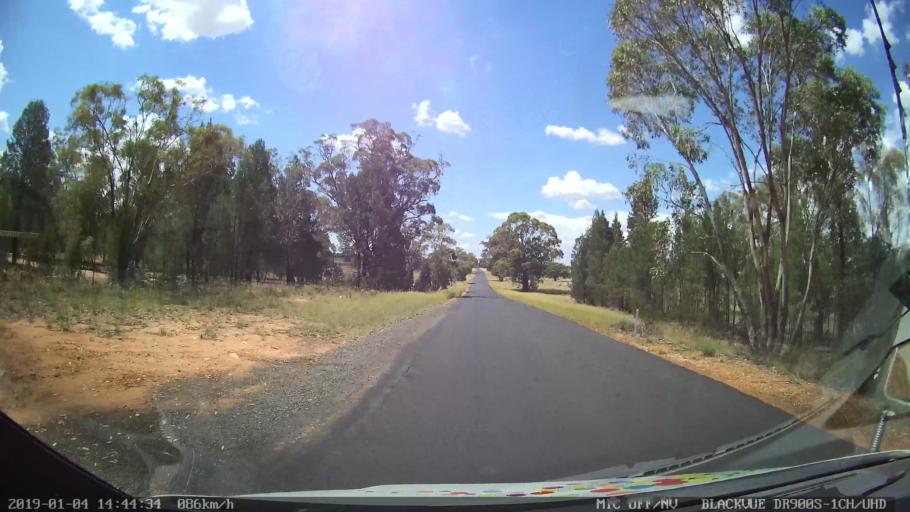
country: AU
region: New South Wales
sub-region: Dubbo Municipality
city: Dubbo
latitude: -32.1047
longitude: 148.6559
